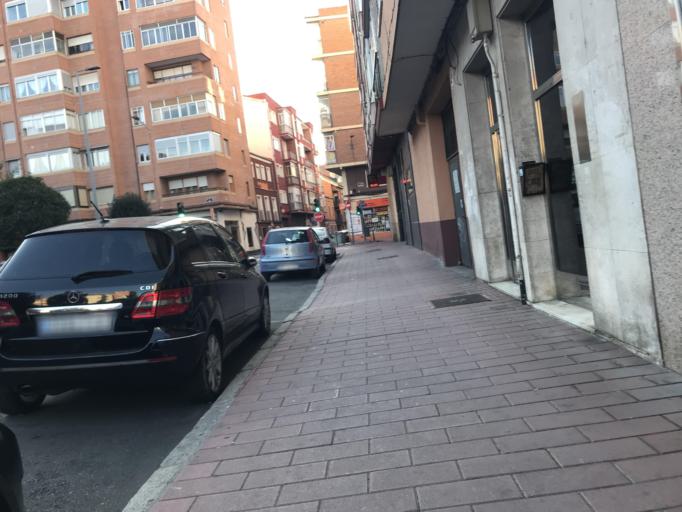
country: ES
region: Castille and Leon
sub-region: Provincia de Valladolid
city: Valladolid
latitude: 41.6498
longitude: -4.7151
